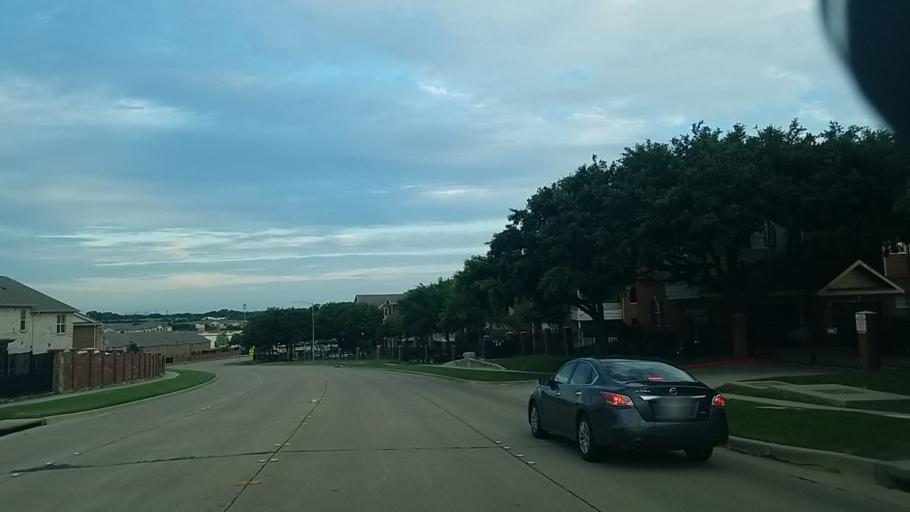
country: US
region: Texas
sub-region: Denton County
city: Lewisville
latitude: 33.0010
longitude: -96.9819
